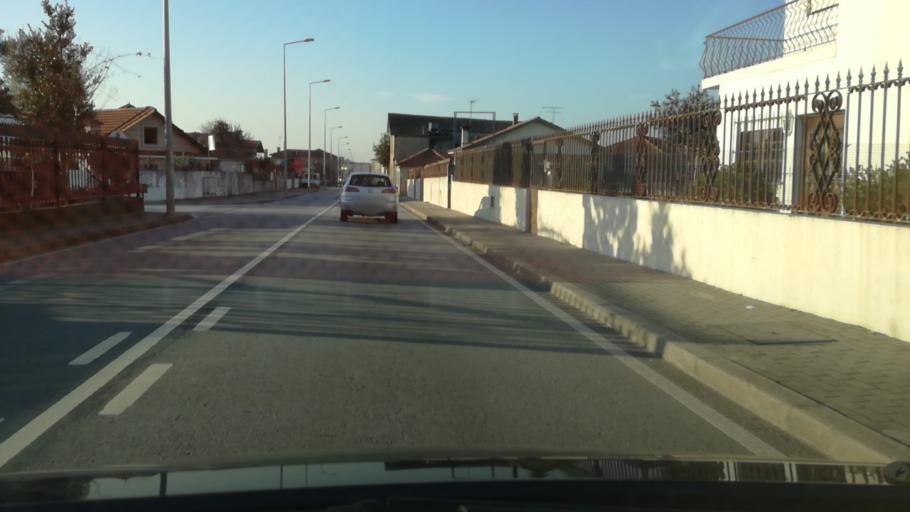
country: PT
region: Porto
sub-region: Trofa
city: Bougado
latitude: 41.3383
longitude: -8.5356
